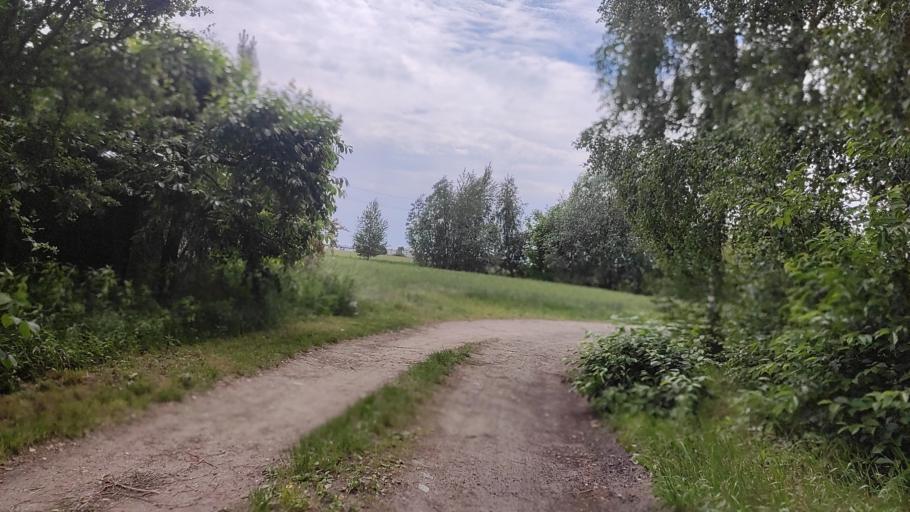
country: PL
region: Greater Poland Voivodeship
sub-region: Powiat poznanski
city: Swarzedz
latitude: 52.3953
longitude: 17.0811
